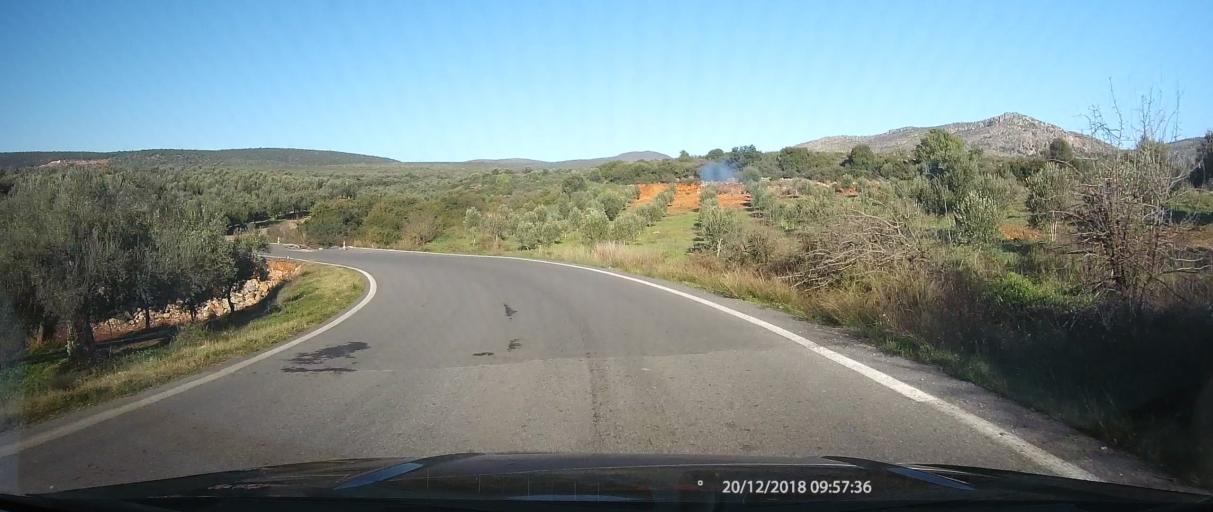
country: GR
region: Peloponnese
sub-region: Nomos Lakonias
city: Yerakion
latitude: 37.0233
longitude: 22.5939
